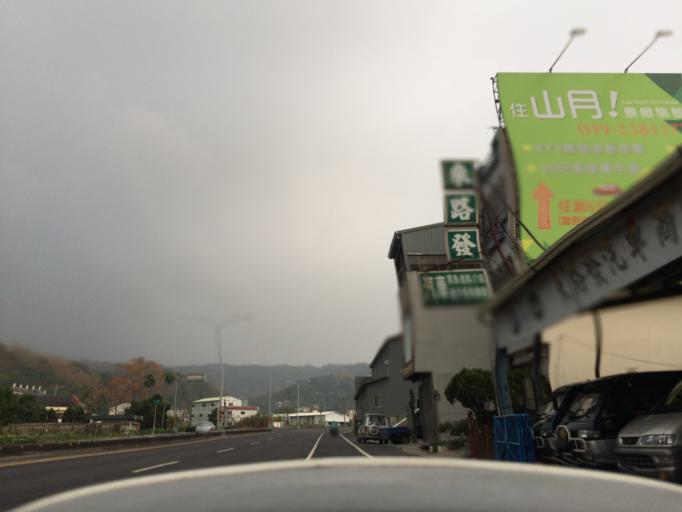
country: TW
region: Taiwan
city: Zhongxing New Village
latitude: 24.0328
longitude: 120.6948
